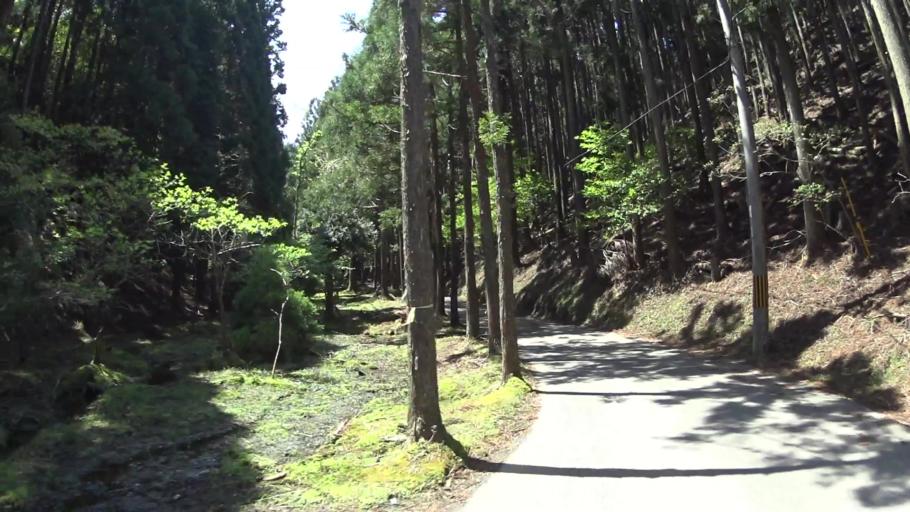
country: JP
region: Shiga Prefecture
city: Kitahama
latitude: 35.1602
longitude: 135.8011
